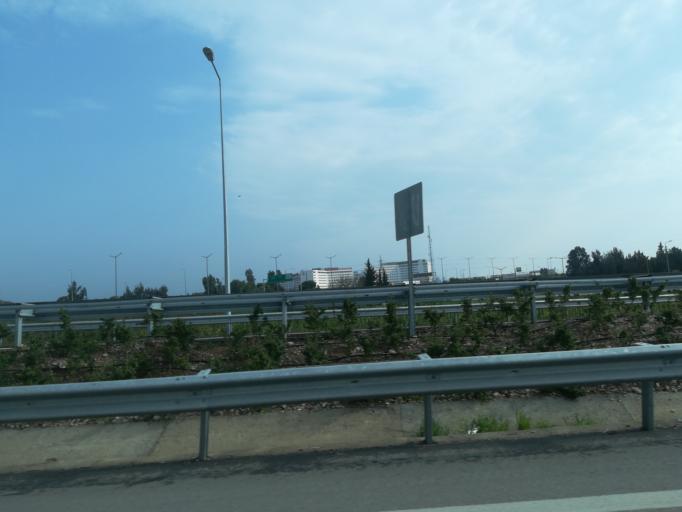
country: TR
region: Adana
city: Adana
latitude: 37.0220
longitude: 35.3415
